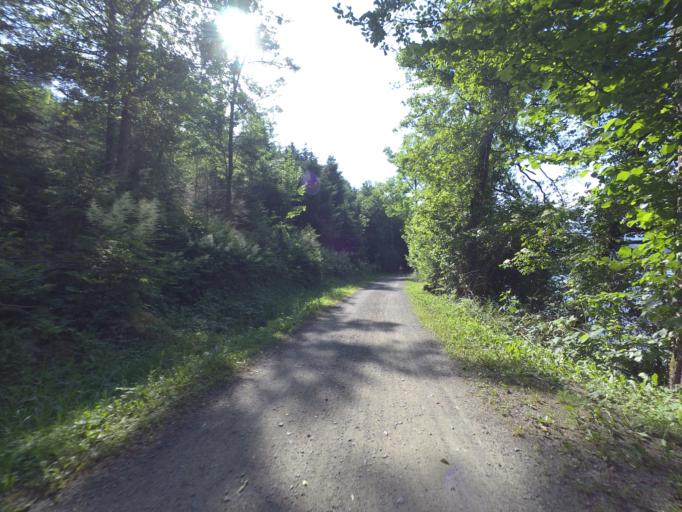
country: AT
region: Carinthia
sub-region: Politischer Bezirk Spittal an der Drau
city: Millstatt
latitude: 46.7980
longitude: 13.5567
